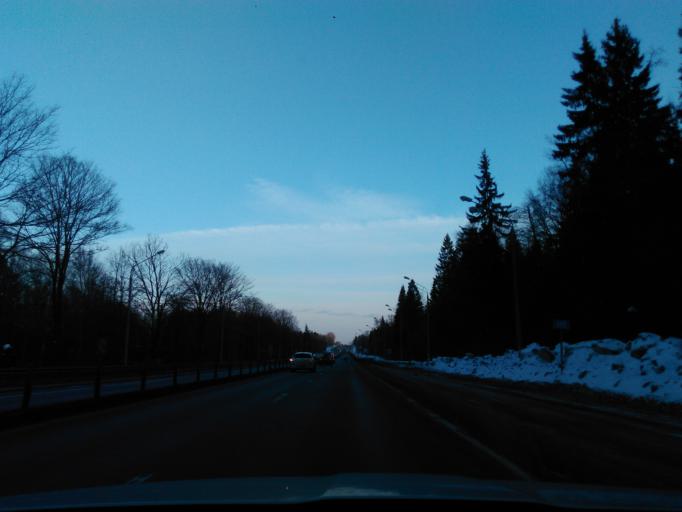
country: RU
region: Moskovskaya
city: Shevlyakovo
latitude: 56.2586
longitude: 36.8628
